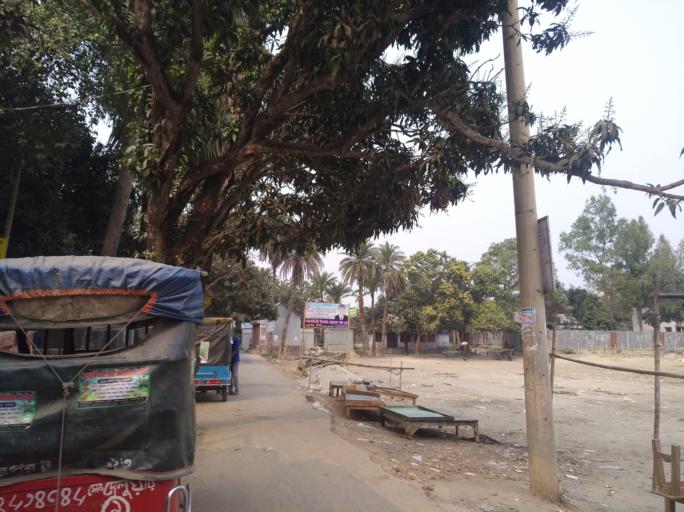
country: BD
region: Dhaka
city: Nagarpur
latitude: 23.9998
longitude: 89.8016
